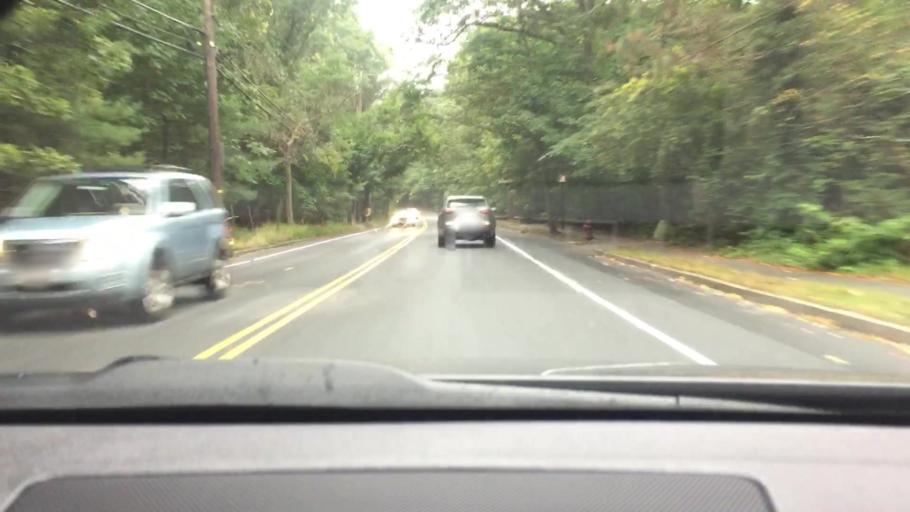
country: US
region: Massachusetts
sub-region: Middlesex County
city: Newton
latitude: 42.3036
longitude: -71.2055
